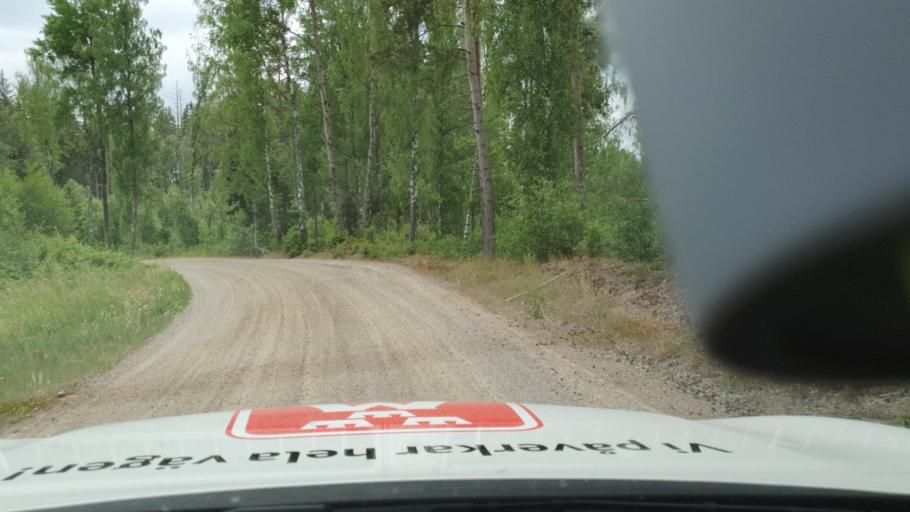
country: SE
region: Vaestra Goetaland
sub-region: Tidaholms Kommun
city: Olofstorp
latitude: 58.1783
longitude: 14.1032
